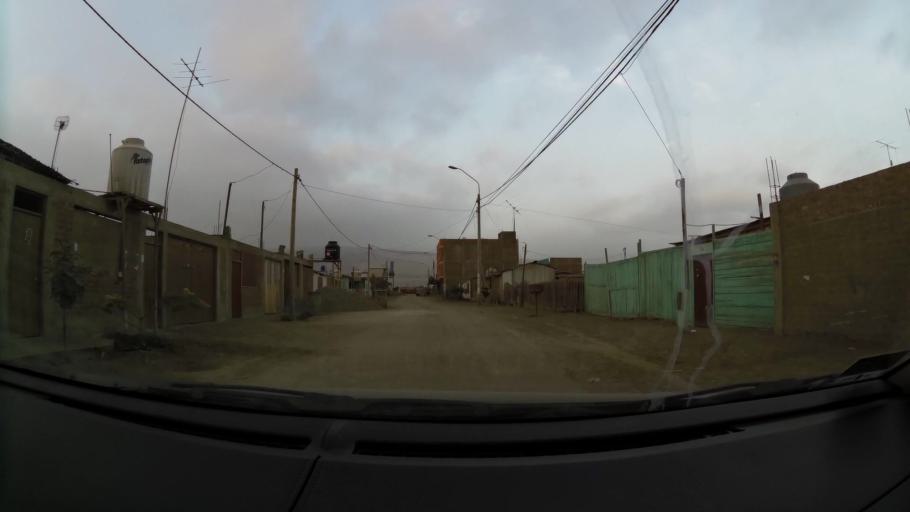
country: PE
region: Lima
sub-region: Lima
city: Santa Rosa
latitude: -11.7326
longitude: -77.1402
